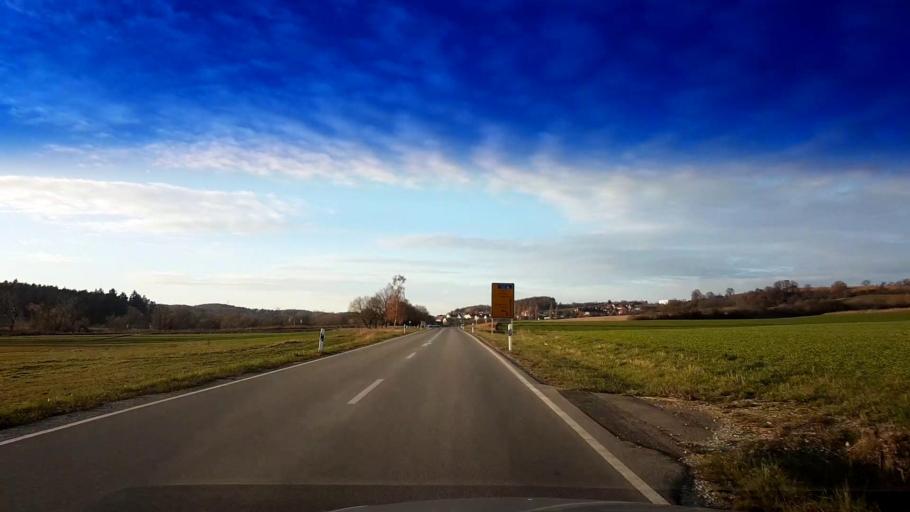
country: DE
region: Bavaria
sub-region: Upper Franconia
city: Priesendorf
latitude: 49.8887
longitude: 10.7414
